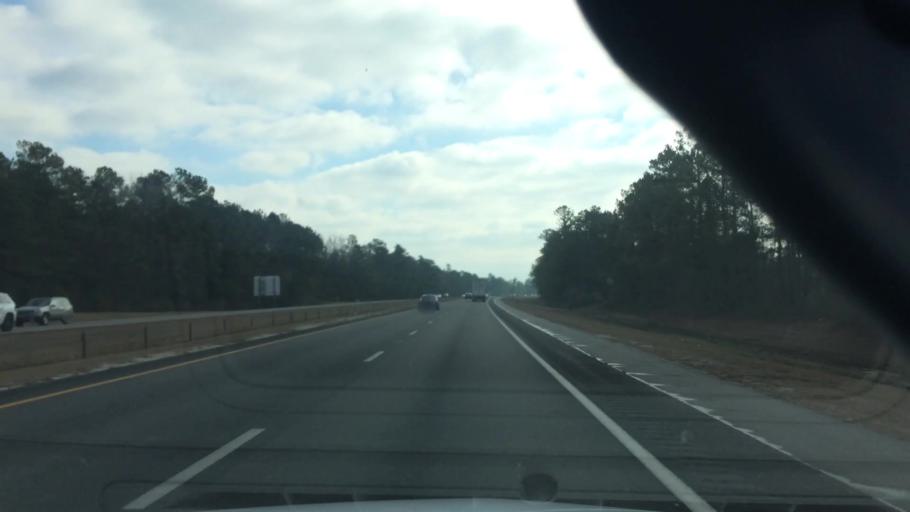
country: US
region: North Carolina
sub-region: Pender County
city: Burgaw
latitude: 34.5649
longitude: -77.8975
